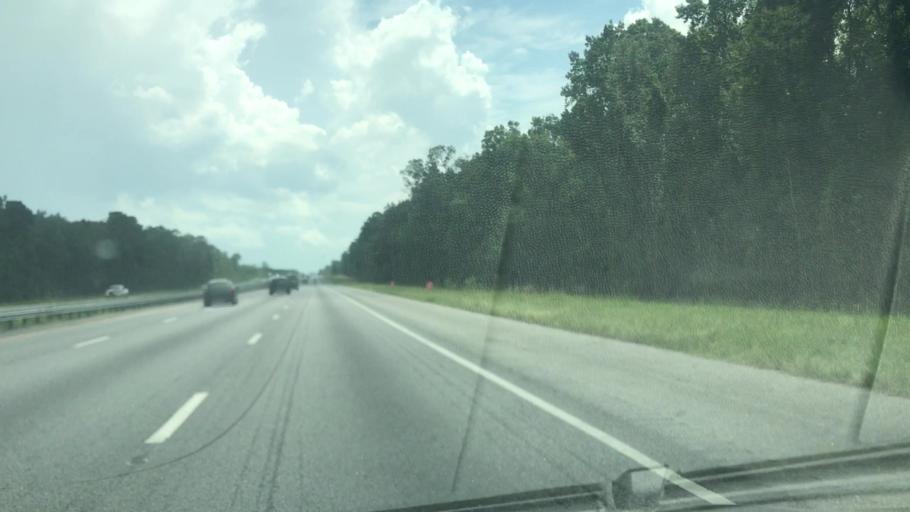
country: US
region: Georgia
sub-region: Liberty County
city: Midway
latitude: 31.6296
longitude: -81.4072
